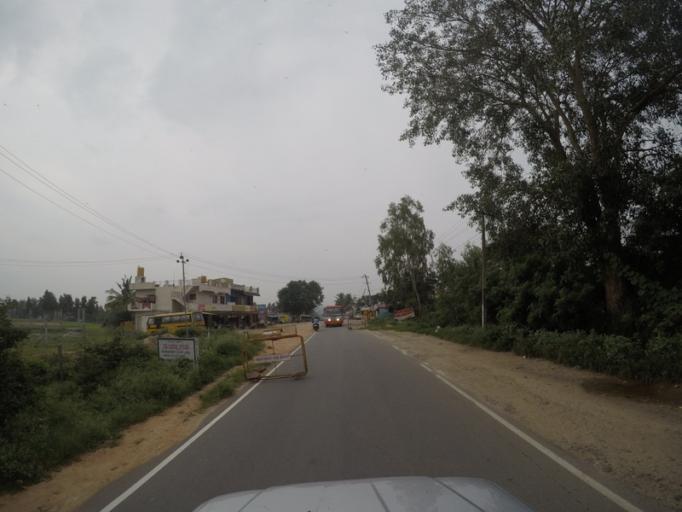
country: IN
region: Karnataka
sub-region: Hassan
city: Belur
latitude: 13.2591
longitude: 75.8490
